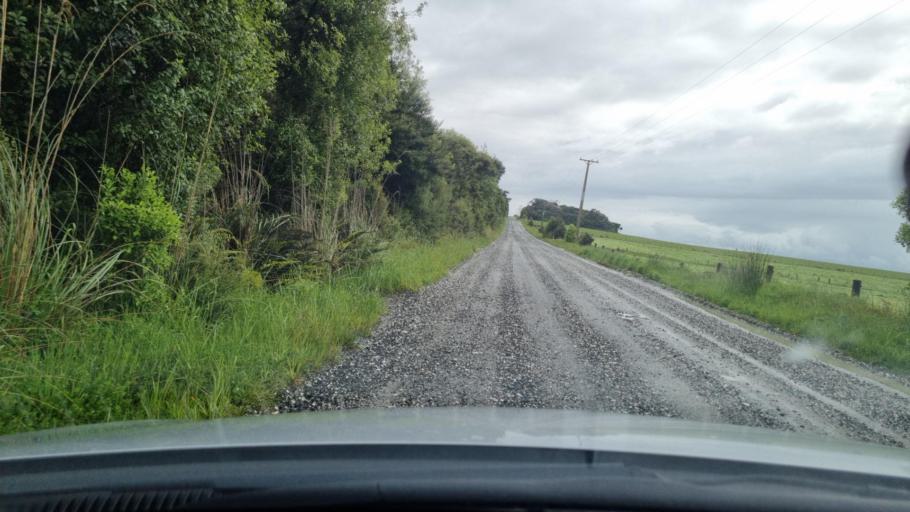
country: NZ
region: Southland
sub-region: Invercargill City
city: Bluff
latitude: -46.5318
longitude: 168.2676
